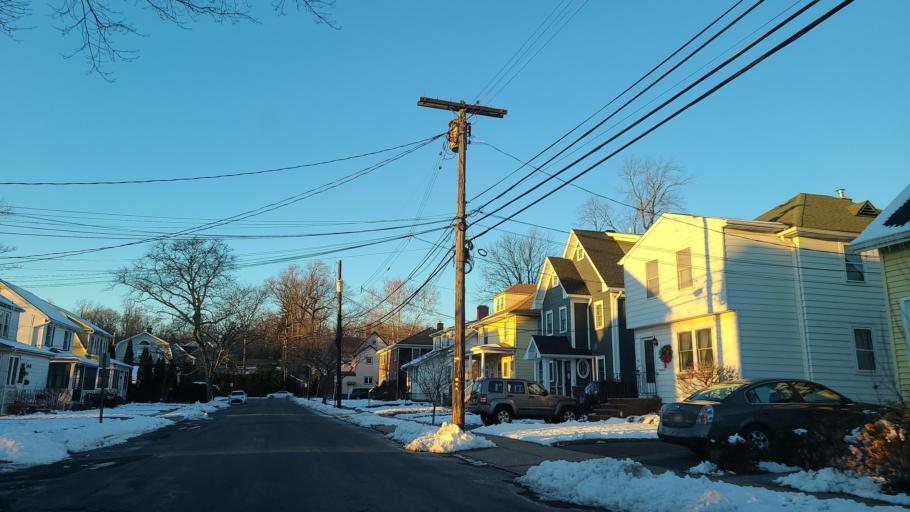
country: US
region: New Jersey
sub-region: Union County
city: Springfield
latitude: 40.7215
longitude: -74.3119
